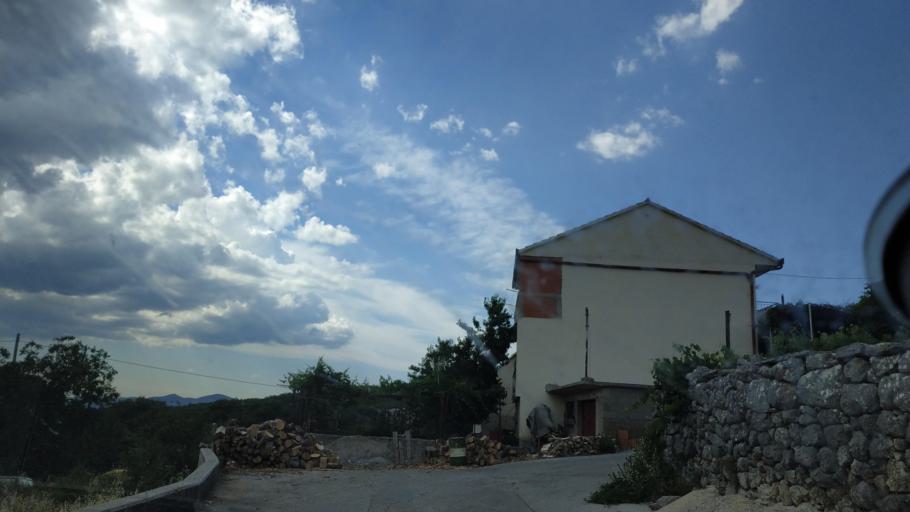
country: HR
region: Splitsko-Dalmatinska
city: Dugopolje
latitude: 43.5637
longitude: 16.6544
